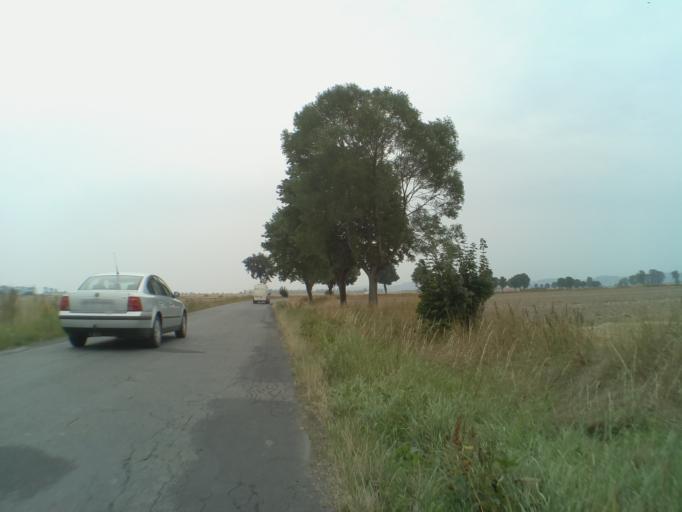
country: PL
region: Lower Silesian Voivodeship
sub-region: Powiat swidnicki
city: Swiebodzice
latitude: 50.8946
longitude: 16.3217
